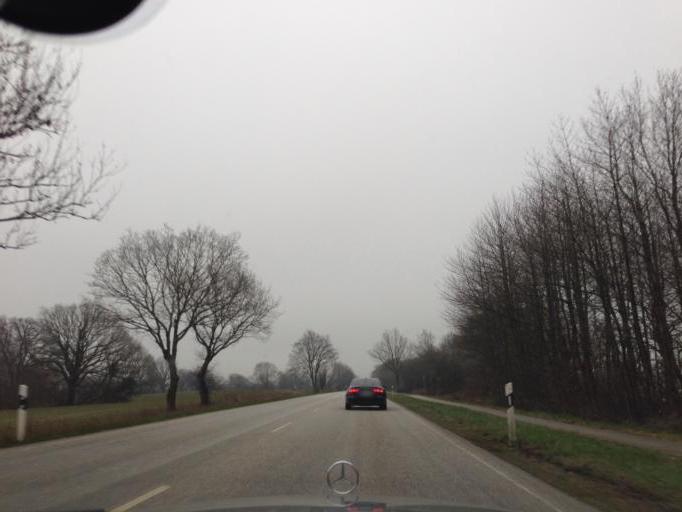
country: DE
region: Schleswig-Holstein
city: Warnau
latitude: 54.1951
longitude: 10.1586
